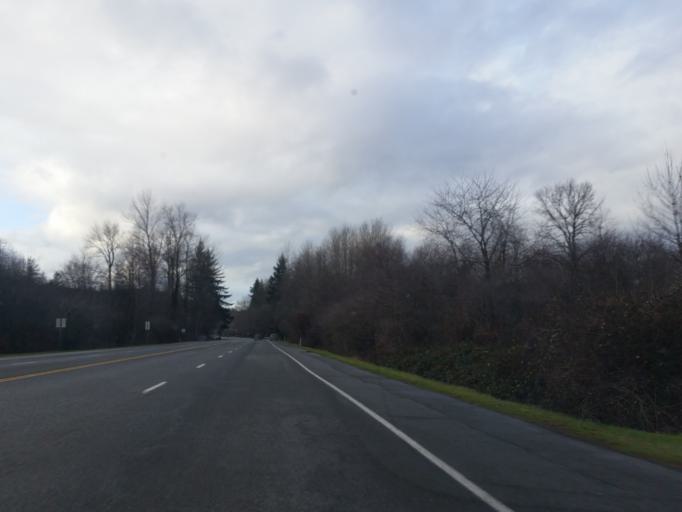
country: US
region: Washington
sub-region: King County
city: North Bend
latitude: 47.5022
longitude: -121.8010
